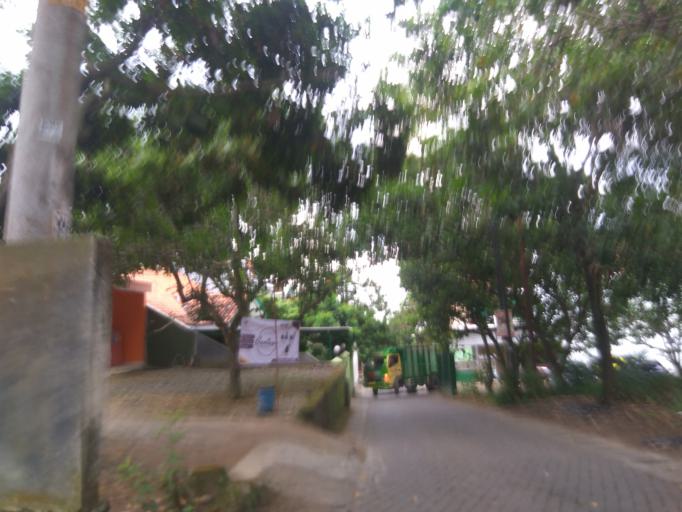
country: ID
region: Central Java
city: Semarang
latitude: -7.0643
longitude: 110.4425
